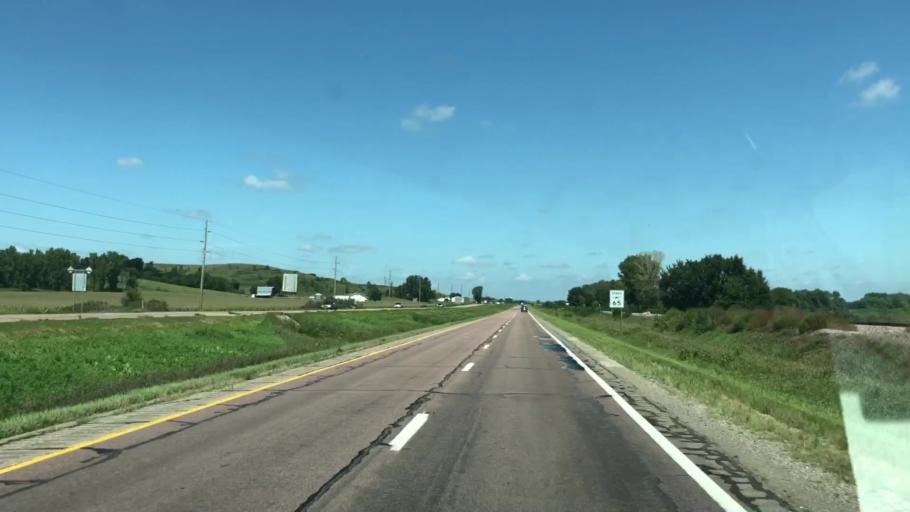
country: US
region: Iowa
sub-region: Woodbury County
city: Sioux City
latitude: 42.6358
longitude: -96.2894
